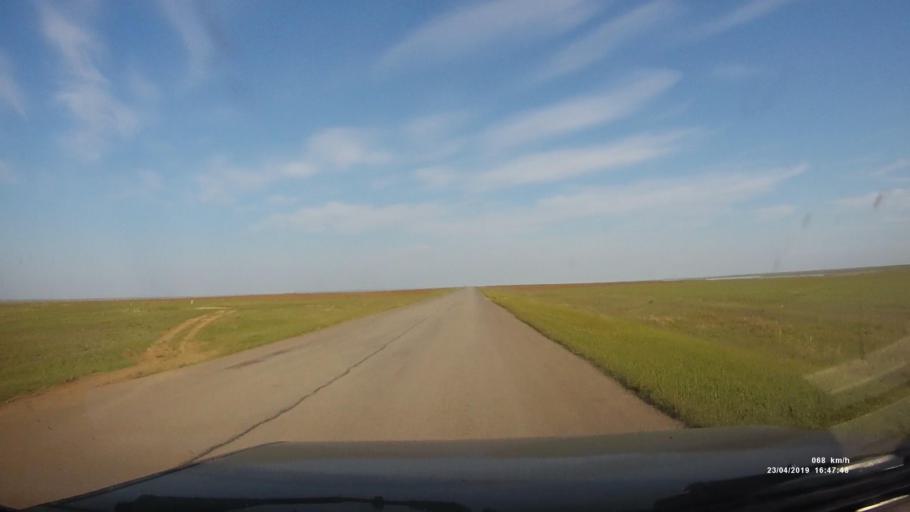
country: RU
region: Kalmykiya
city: Priyutnoye
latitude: 46.3374
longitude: 43.2529
